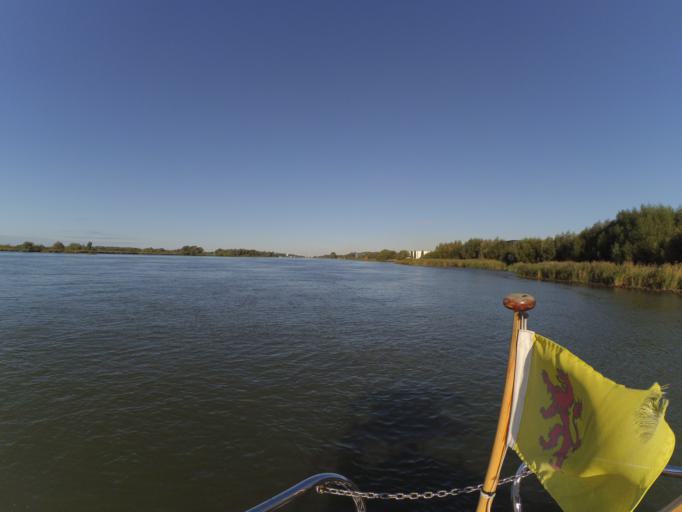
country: NL
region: South Holland
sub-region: Gemeente Zwijndrecht
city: Zwijndrecht
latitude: 51.8045
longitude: 4.6099
